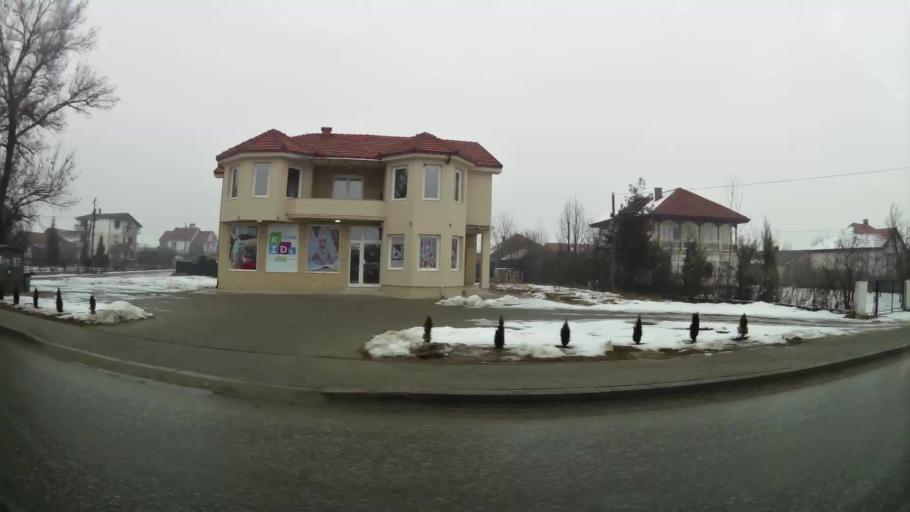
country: MK
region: Petrovec
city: Petrovec
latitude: 41.9347
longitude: 21.6210
